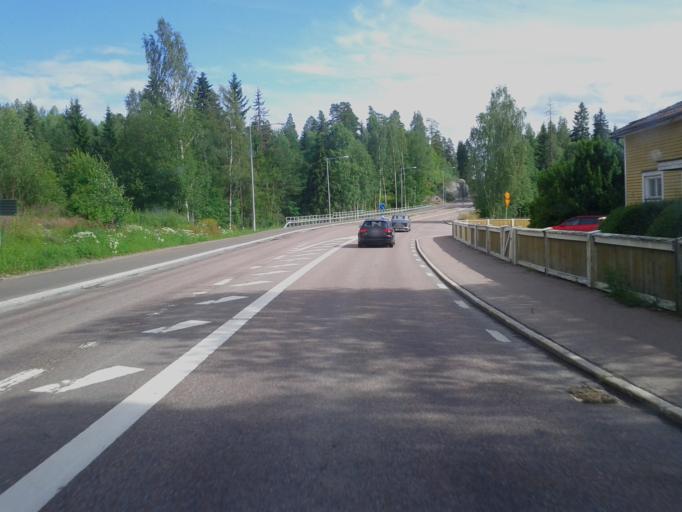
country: SE
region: Dalarna
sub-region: Faluns Kommun
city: Grycksbo
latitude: 60.6809
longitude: 15.5057
